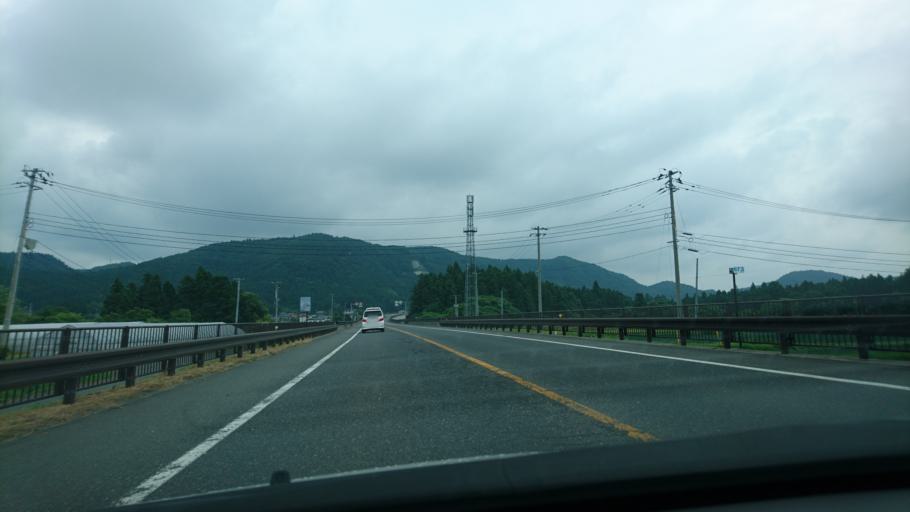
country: JP
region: Miyagi
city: Furukawa
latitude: 38.7331
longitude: 140.7793
